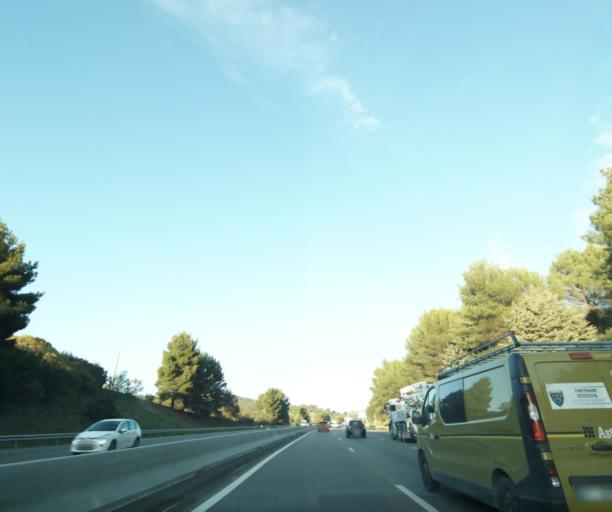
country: FR
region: Provence-Alpes-Cote d'Azur
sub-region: Departement des Bouches-du-Rhone
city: Roquevaire
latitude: 43.3421
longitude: 5.6107
